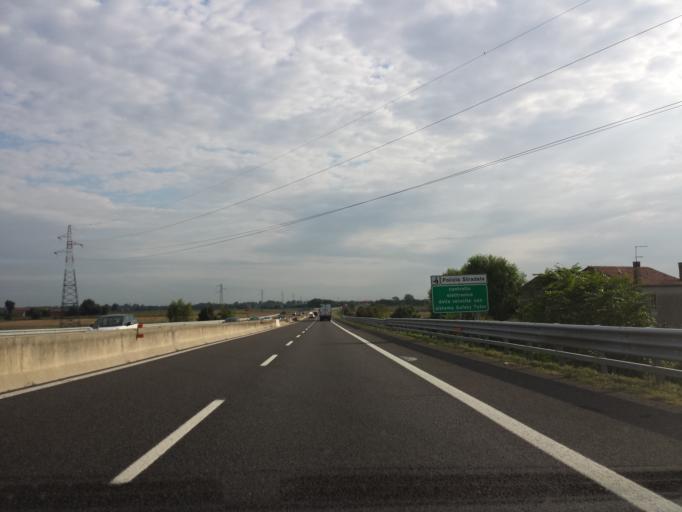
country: IT
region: Veneto
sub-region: Provincia di Padova
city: Stanghella
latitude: 45.1386
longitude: 11.7749
